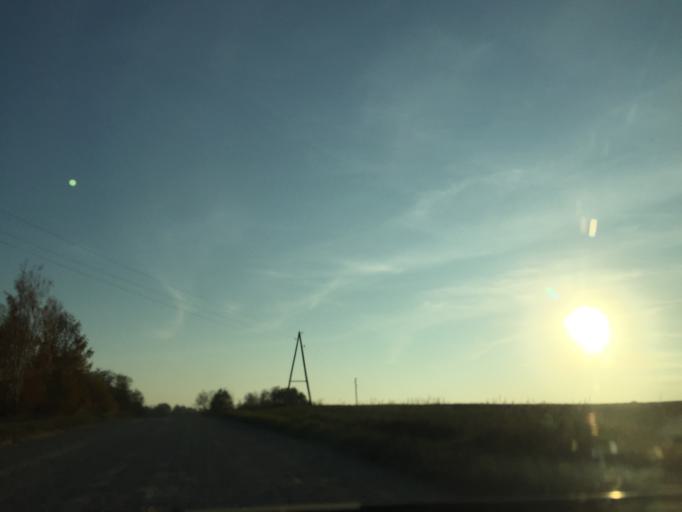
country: LV
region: Vainode
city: Vainode
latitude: 56.5608
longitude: 21.8441
